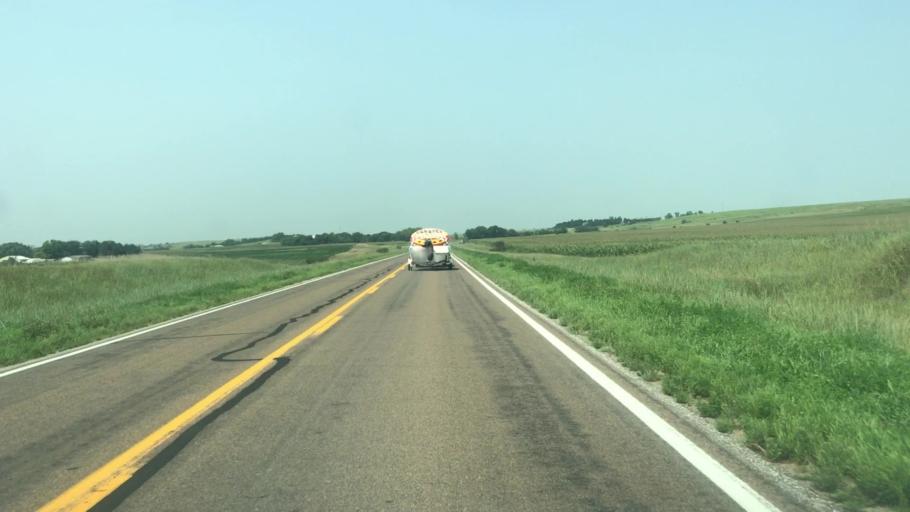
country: US
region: Nebraska
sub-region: Sherman County
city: Loup City
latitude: 41.2514
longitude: -98.9391
